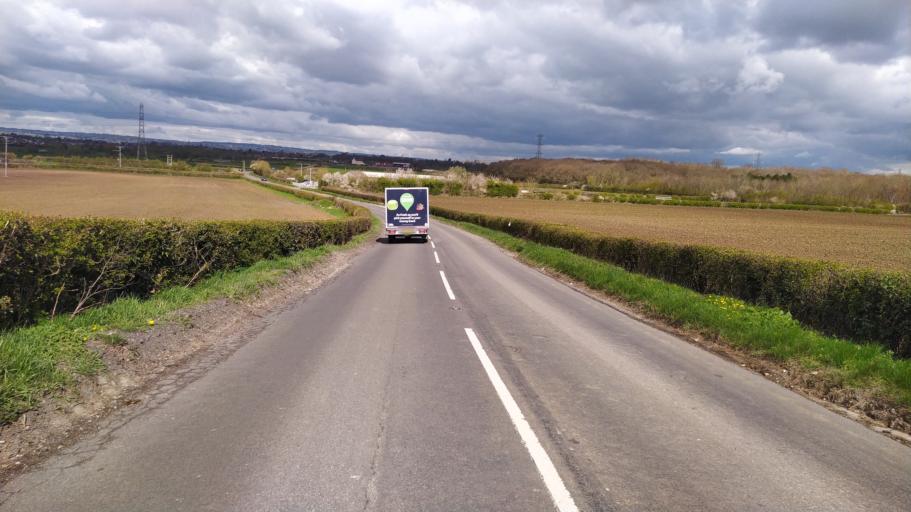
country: GB
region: England
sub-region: Wiltshire
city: North Bradley
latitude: 51.3025
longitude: -2.1794
